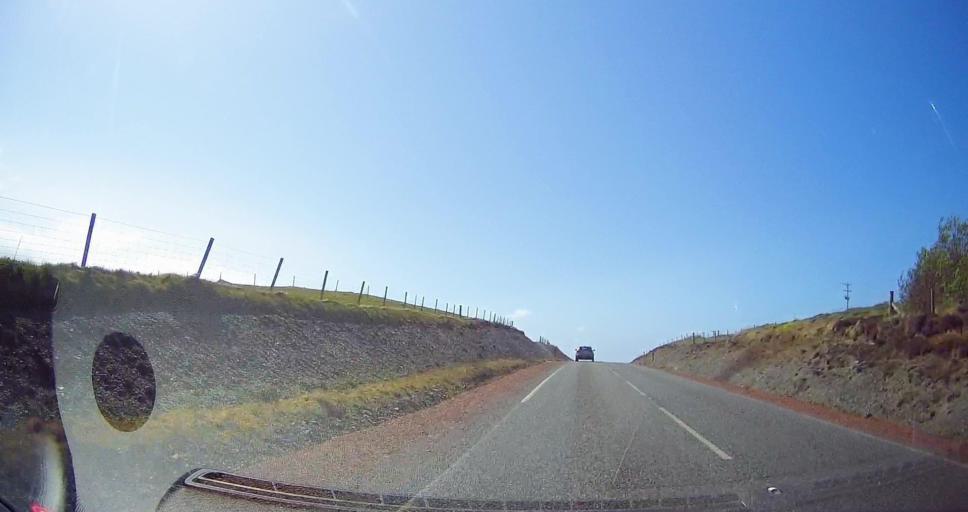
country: GB
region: Scotland
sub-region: Shetland Islands
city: Sandwick
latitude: 60.1225
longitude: -1.2868
